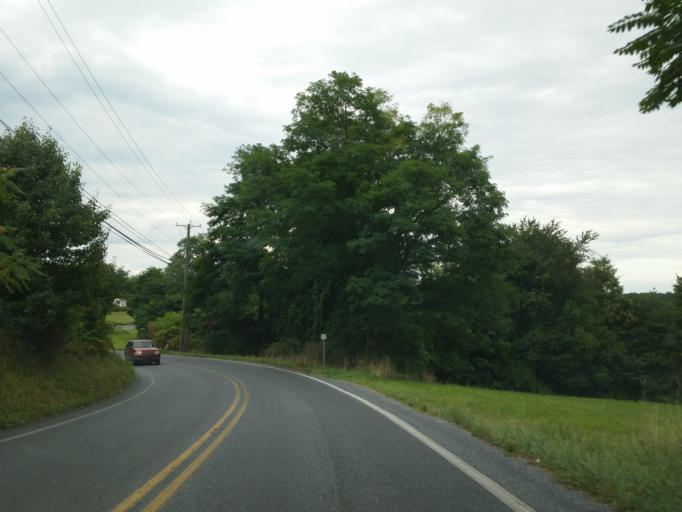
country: US
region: Pennsylvania
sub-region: Berks County
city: Alleghenyville
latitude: 40.2467
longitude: -76.0113
